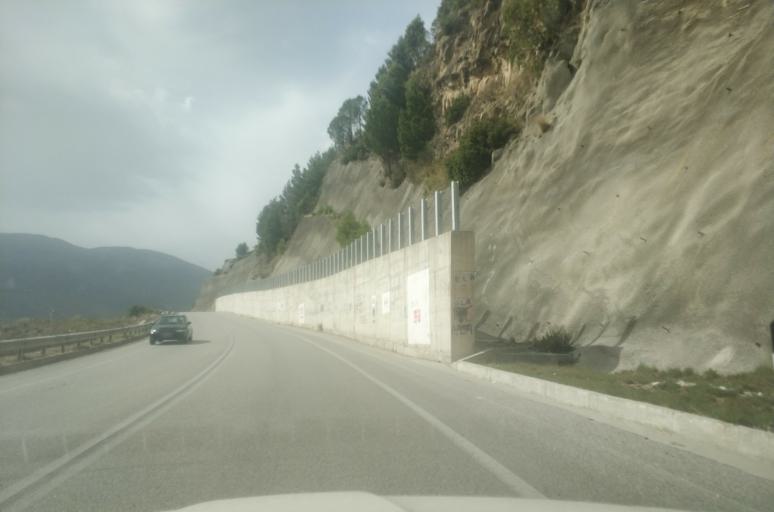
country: AL
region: Gjirokaster
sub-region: Rrethi i Tepelenes
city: Memaliaj
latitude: 40.3532
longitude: 19.9669
